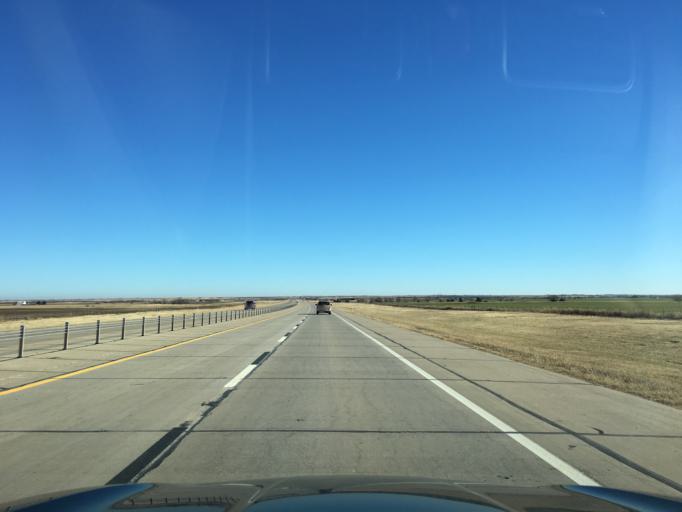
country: US
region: Oklahoma
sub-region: Noble County
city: Perry
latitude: 36.3991
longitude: -97.2961
